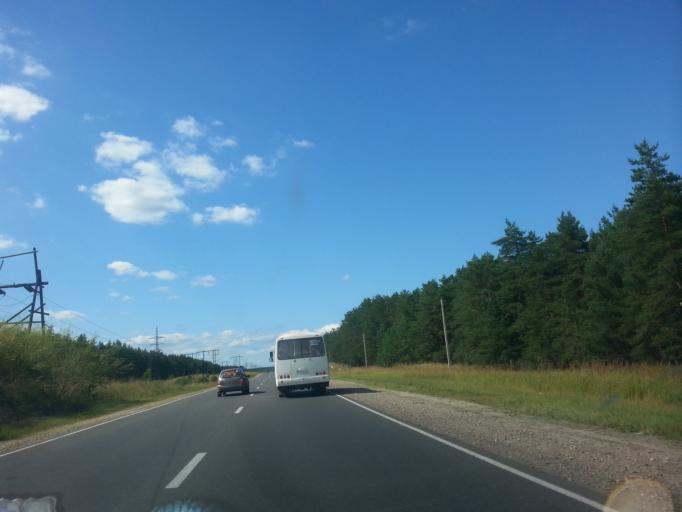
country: RU
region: Nizjnij Novgorod
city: Lukino
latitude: 56.3944
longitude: 43.6817
